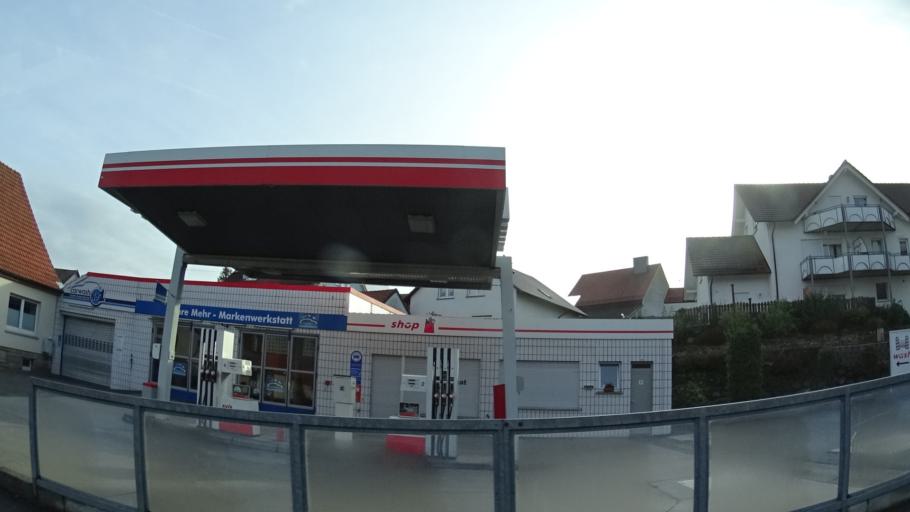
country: DE
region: Hesse
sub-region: Regierungsbezirk Kassel
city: Hosenfeld
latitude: 50.5041
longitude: 9.4794
